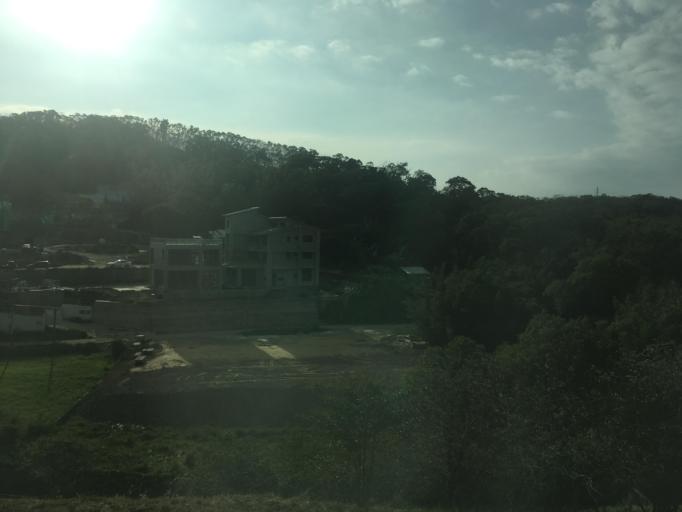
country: TW
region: Taiwan
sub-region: Miaoli
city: Miaoli
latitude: 24.6146
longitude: 120.8466
